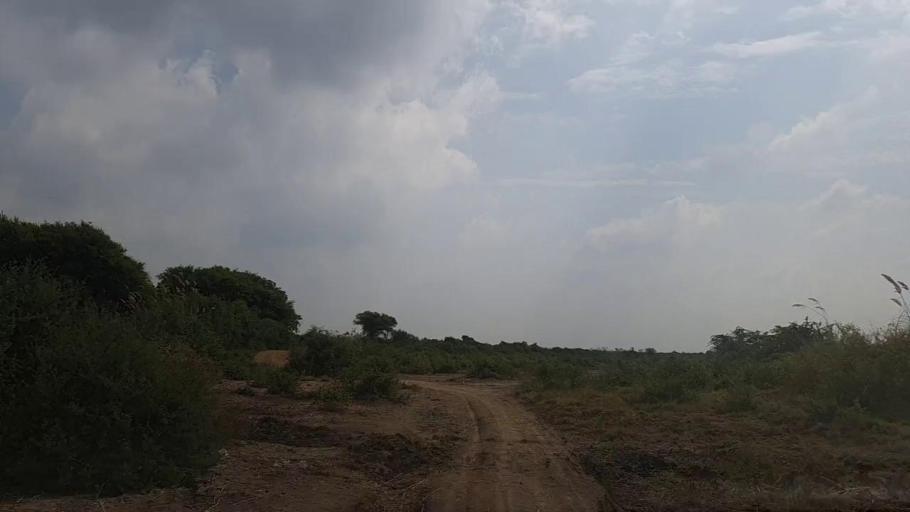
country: PK
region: Sindh
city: Mirpur Batoro
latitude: 24.6092
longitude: 68.1379
